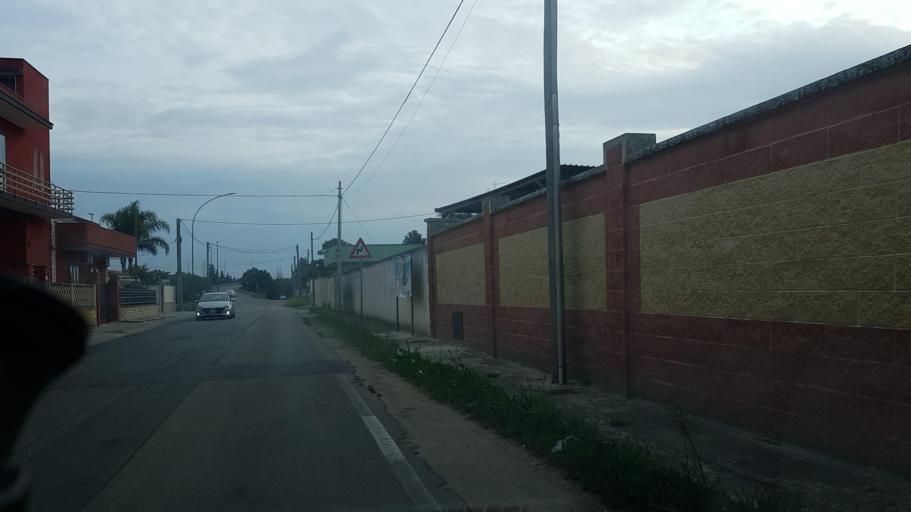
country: IT
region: Apulia
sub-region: Provincia di Lecce
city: Trepuzzi
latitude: 40.4158
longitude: 18.0736
